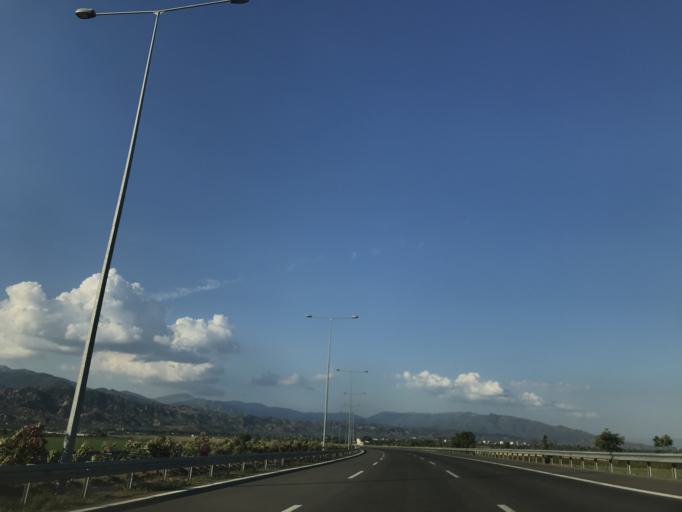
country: TR
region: Aydin
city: Tepecik
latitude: 37.8247
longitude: 27.9136
